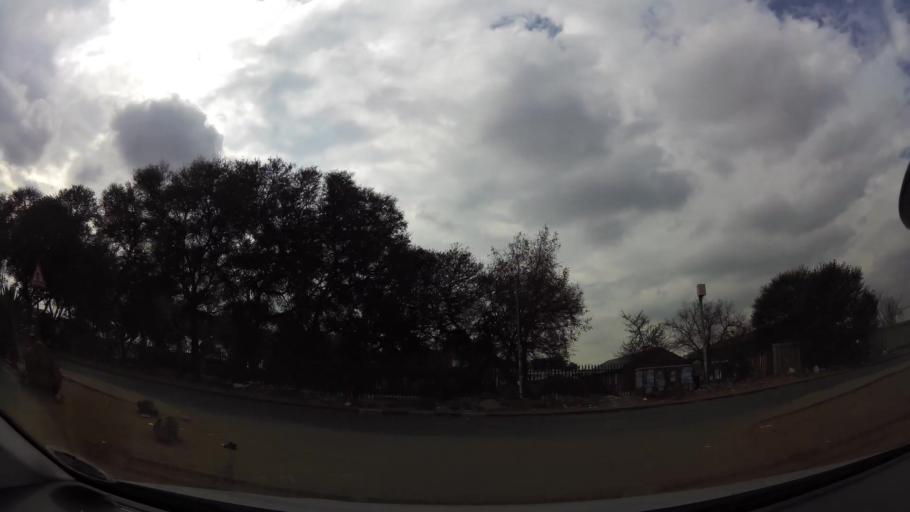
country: ZA
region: Gauteng
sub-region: City of Johannesburg Metropolitan Municipality
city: Soweto
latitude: -26.2709
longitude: 27.8554
